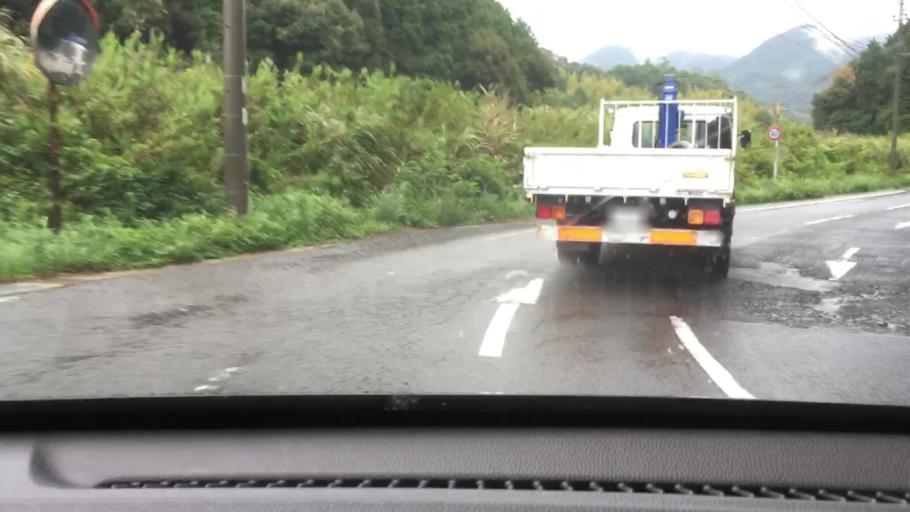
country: JP
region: Nagasaki
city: Togitsu
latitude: 32.8594
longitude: 129.7772
